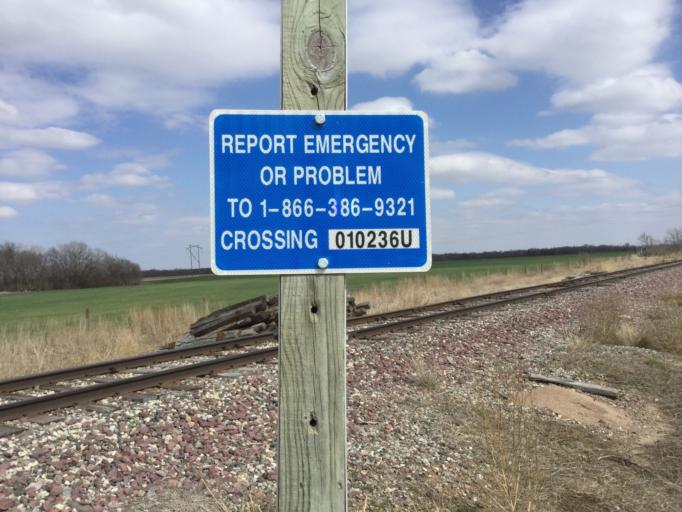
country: US
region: Kansas
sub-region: Barton County
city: Great Bend
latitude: 38.4119
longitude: -98.8668
